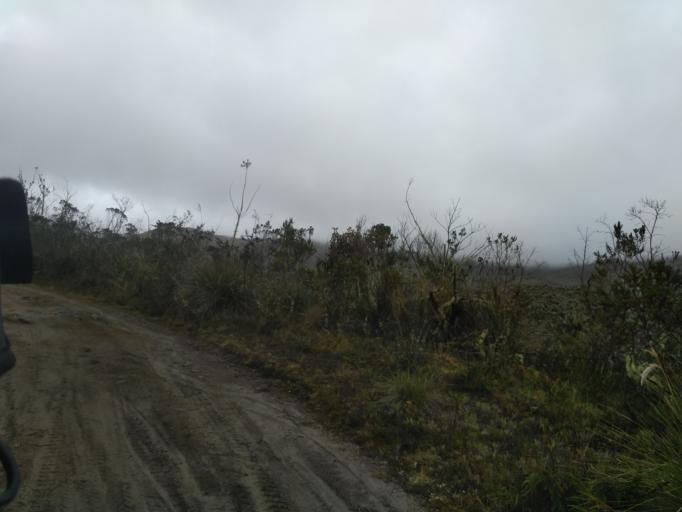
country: EC
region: Carchi
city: San Gabriel
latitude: 0.7068
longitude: -77.8295
